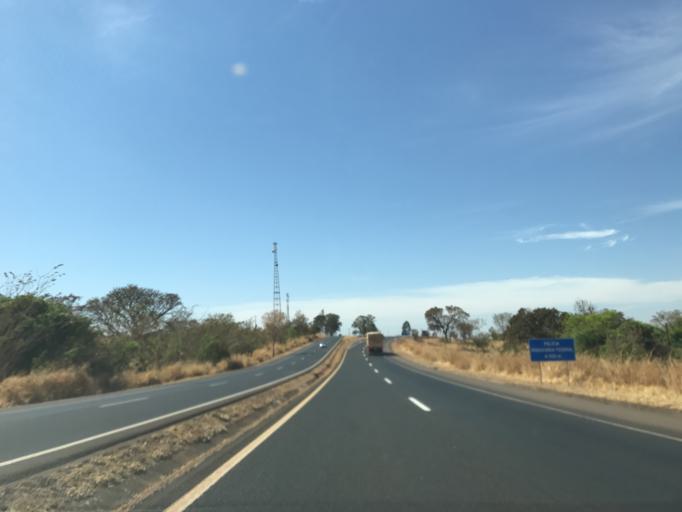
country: BR
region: Minas Gerais
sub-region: Monte Alegre De Minas
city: Monte Alegre de Minas
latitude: -18.8637
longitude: -49.0710
